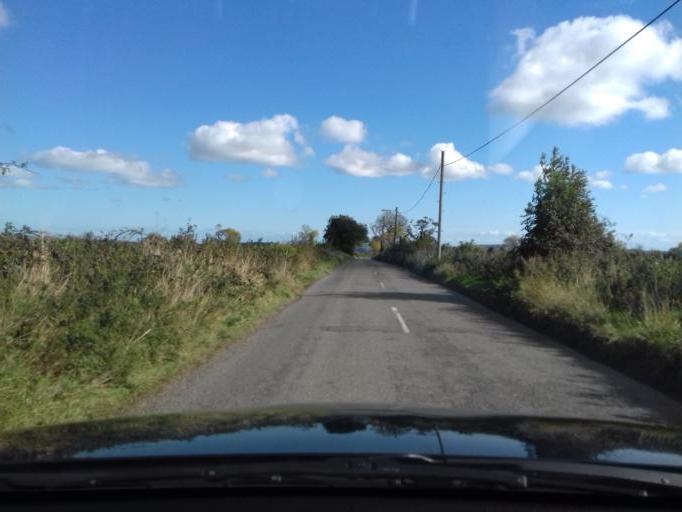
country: IE
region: Leinster
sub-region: An Mhi
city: Slane
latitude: 53.6868
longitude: -6.5272
